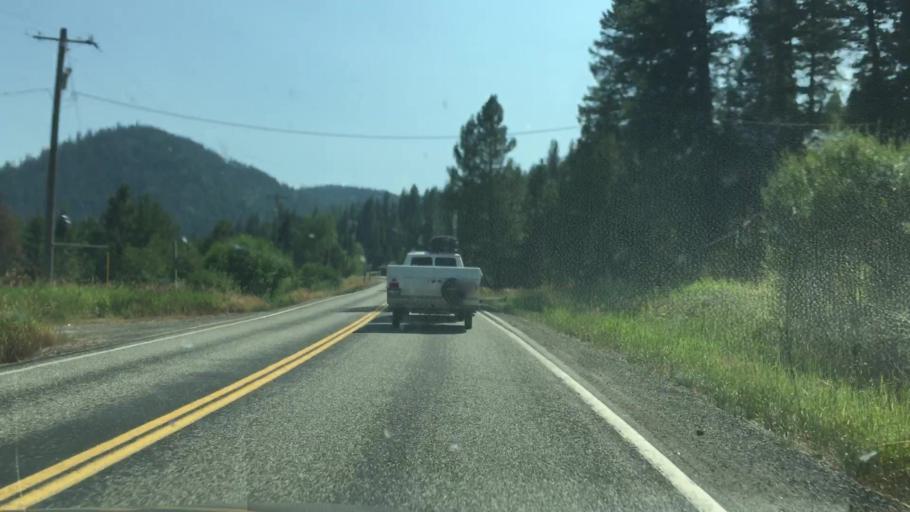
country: US
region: Idaho
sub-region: Valley County
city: Cascade
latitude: 44.3109
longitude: -116.0858
